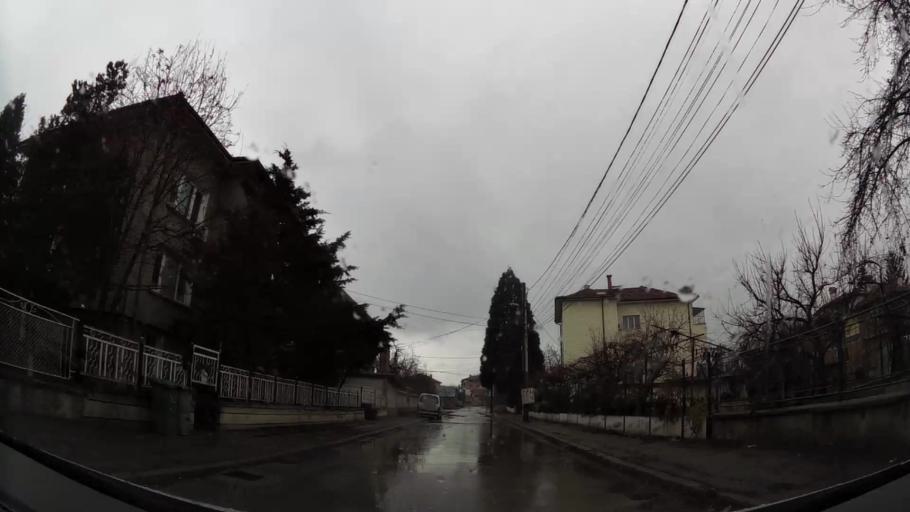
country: BG
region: Sofia-Capital
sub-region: Stolichna Obshtina
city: Sofia
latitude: 42.6311
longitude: 23.4124
